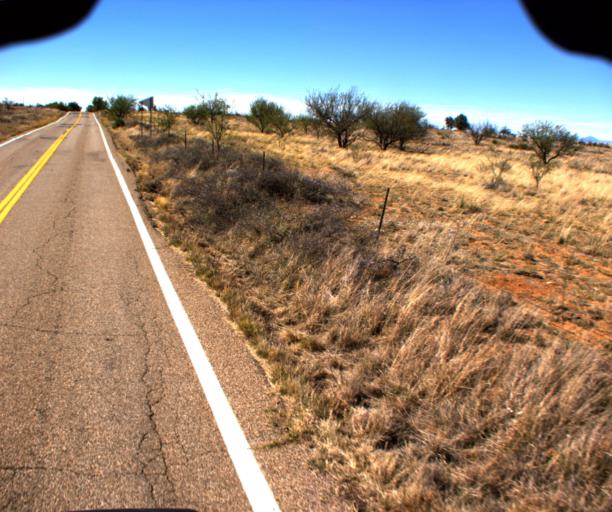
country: US
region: Arizona
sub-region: Cochise County
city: Huachuca City
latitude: 31.5801
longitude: -110.5570
